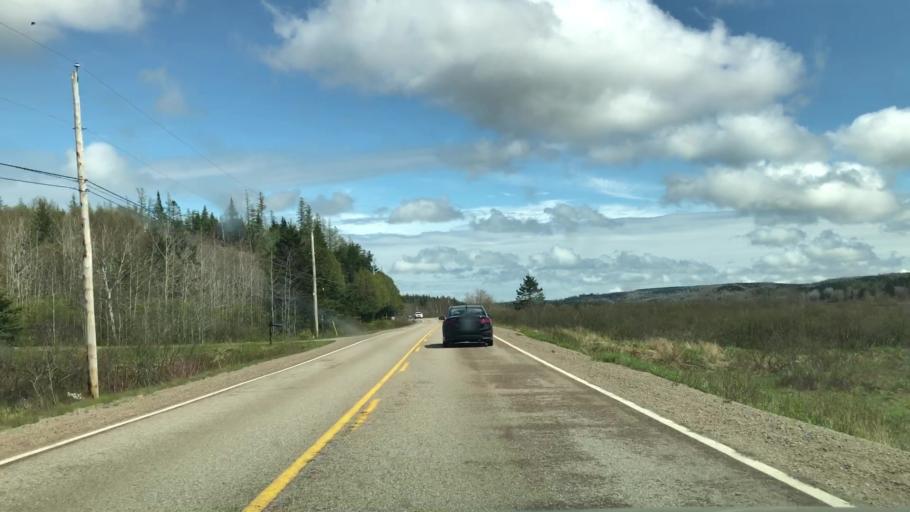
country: CA
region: Nova Scotia
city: Antigonish
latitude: 45.1946
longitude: -61.9985
